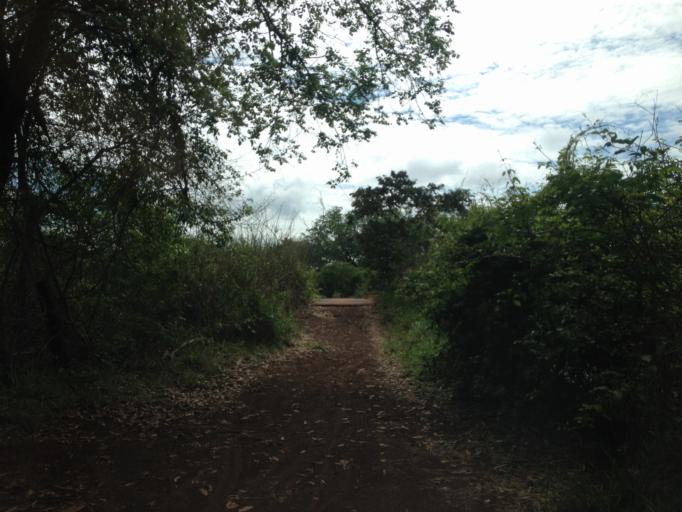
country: BR
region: Minas Gerais
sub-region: Capinopolis
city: Capinopolis
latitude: -18.3492
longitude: -49.6022
